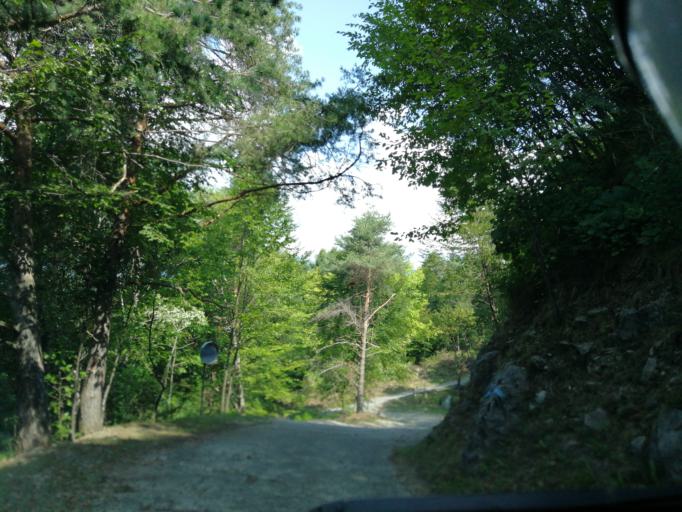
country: IT
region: Trentino-Alto Adige
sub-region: Provincia di Trento
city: Storo
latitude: 45.8296
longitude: 10.5693
